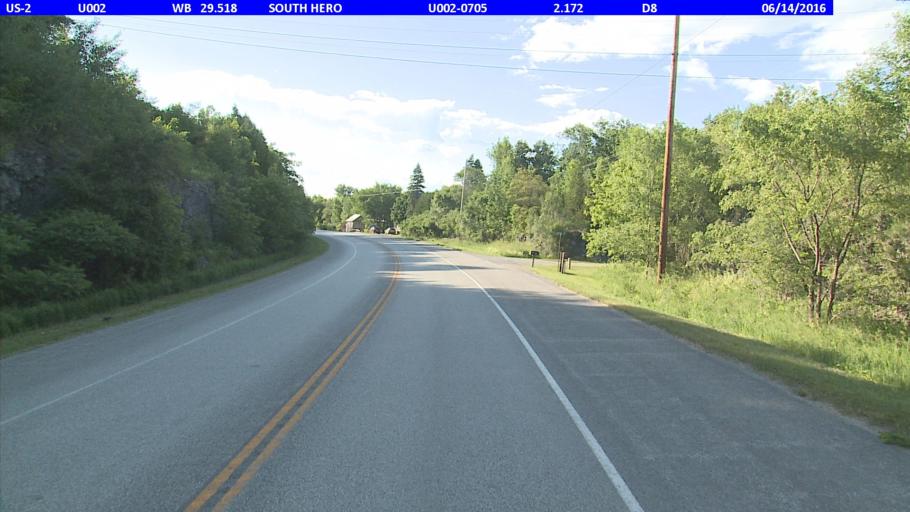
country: US
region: New York
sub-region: Clinton County
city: Cumberland Head
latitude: 44.6508
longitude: -73.3164
